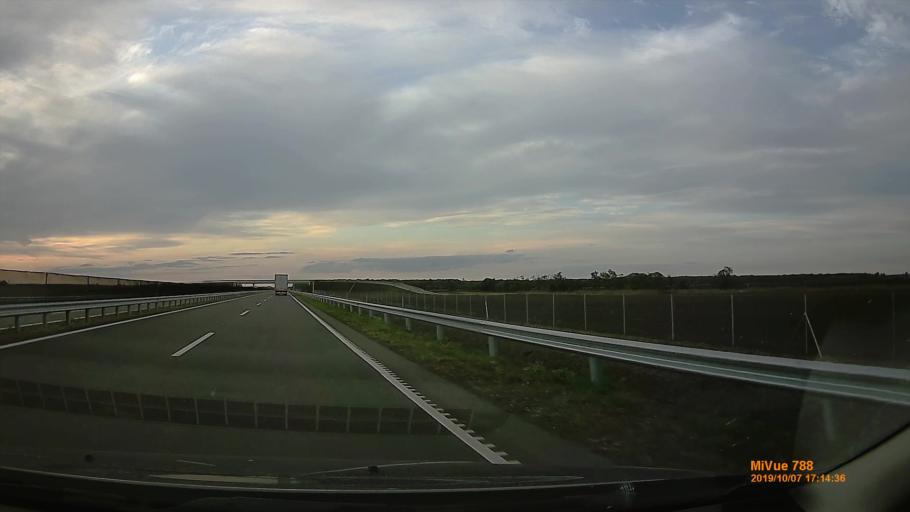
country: HU
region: Jasz-Nagykun-Szolnok
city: Kunszentmarton
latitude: 46.8355
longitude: 20.3461
